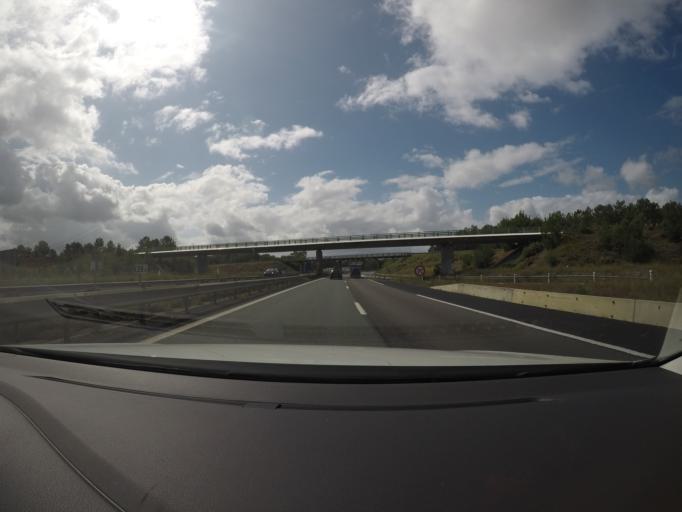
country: FR
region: Aquitaine
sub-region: Departement des Landes
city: Saint-Geours-de-Maremne
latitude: 43.6965
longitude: -1.2305
